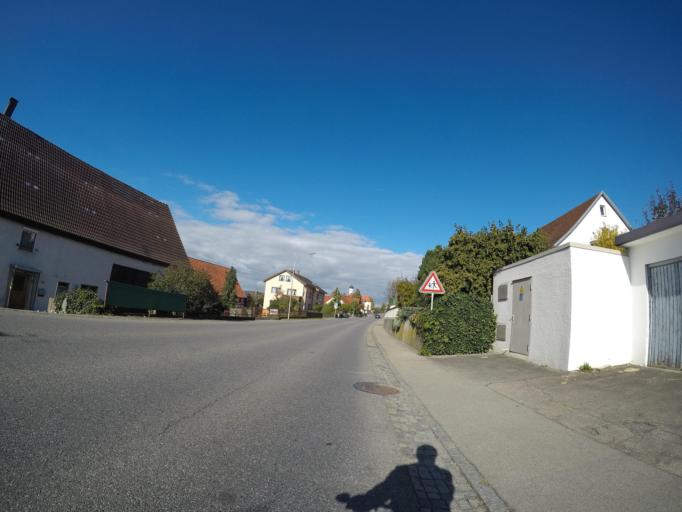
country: DE
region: Baden-Wuerttemberg
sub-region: Tuebingen Region
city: Seekirch
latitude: 48.1255
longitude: 9.6522
